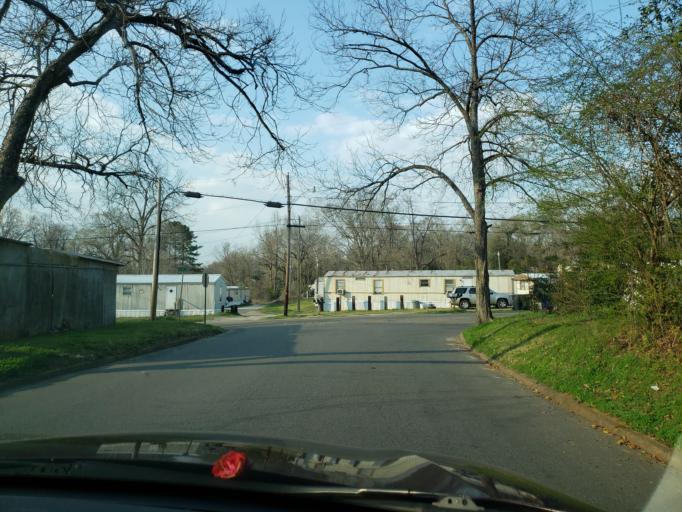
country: US
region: Alabama
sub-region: Hale County
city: Greensboro
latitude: 32.7050
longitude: -87.5983
